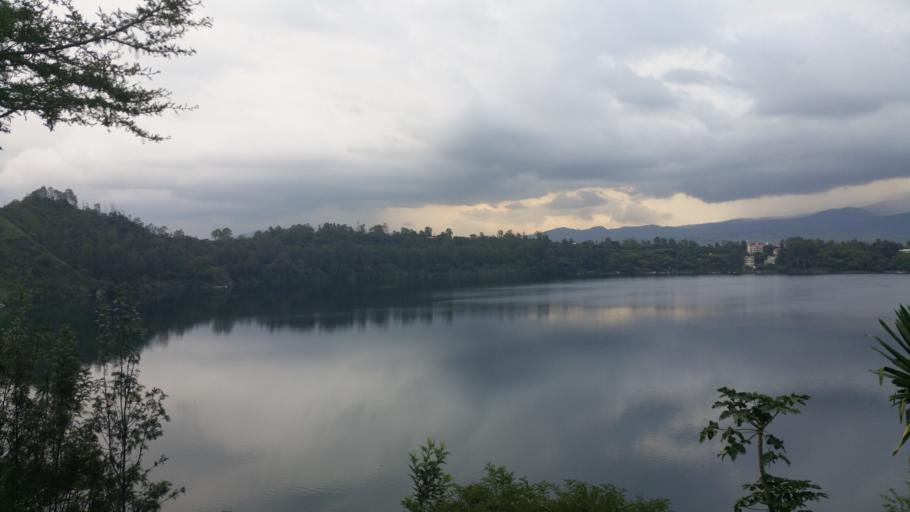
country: ET
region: Oromiya
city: Bishoftu
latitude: 8.7832
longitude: 38.9969
